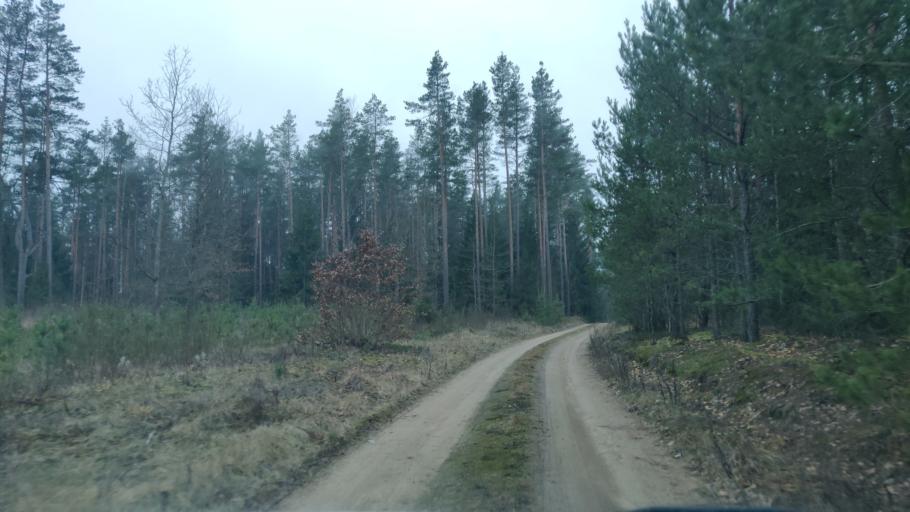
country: LT
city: Trakai
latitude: 54.5573
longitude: 24.9551
